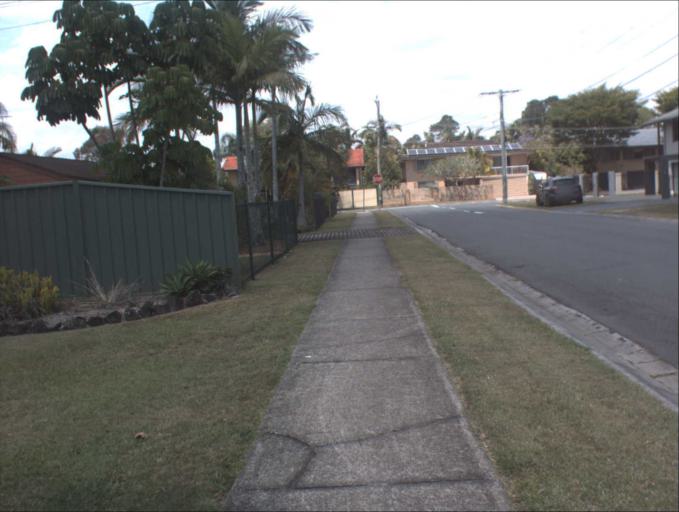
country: AU
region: Queensland
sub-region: Logan
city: Slacks Creek
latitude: -27.6444
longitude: 153.1616
